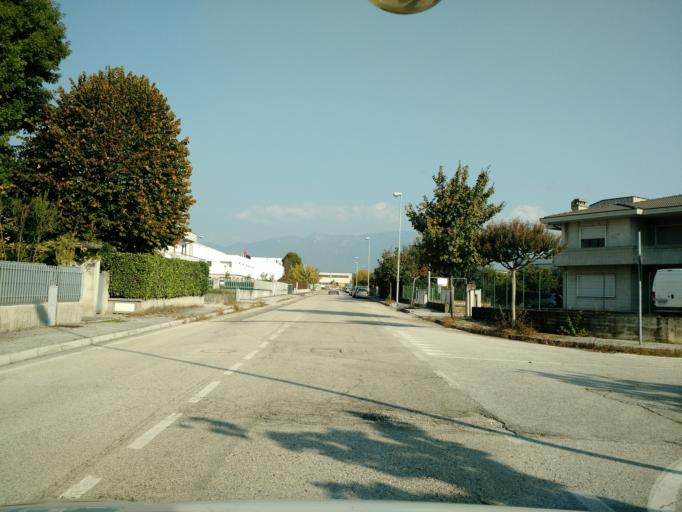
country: IT
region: Veneto
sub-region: Provincia di Vicenza
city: Thiene
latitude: 45.6804
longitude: 11.4707
